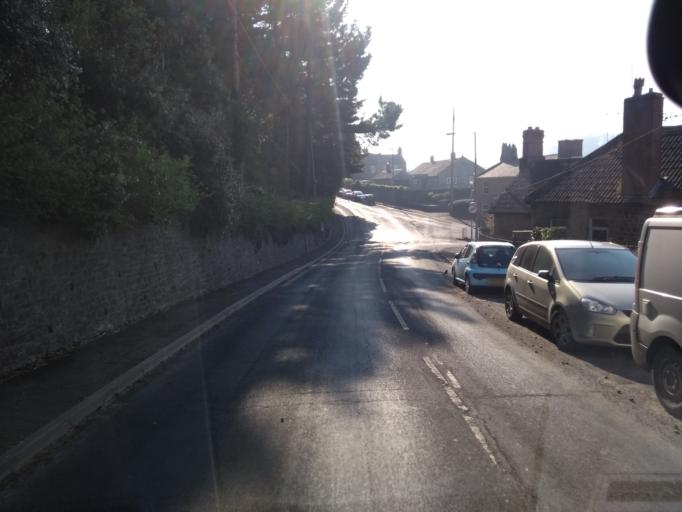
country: GB
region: England
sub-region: Somerset
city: Ilminster
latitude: 50.9275
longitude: -2.9060
